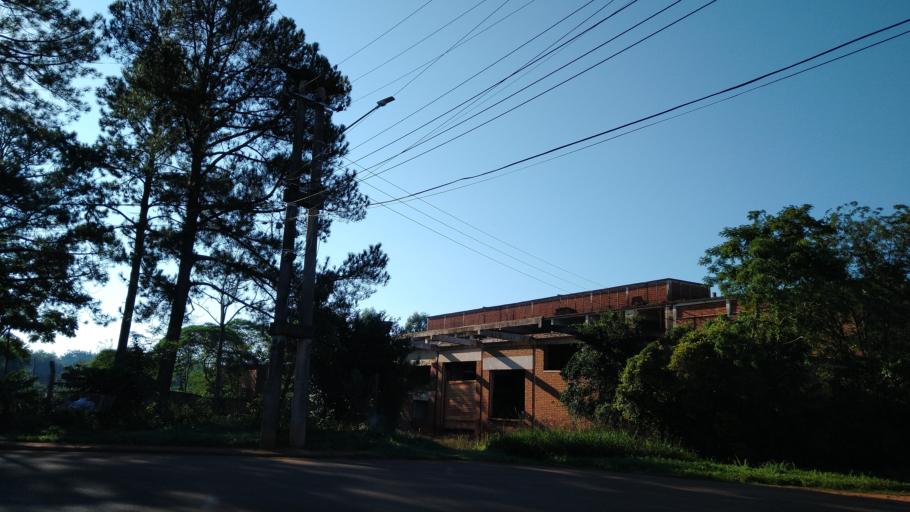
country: AR
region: Misiones
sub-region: Departamento de Montecarlo
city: Montecarlo
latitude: -26.5753
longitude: -54.7455
